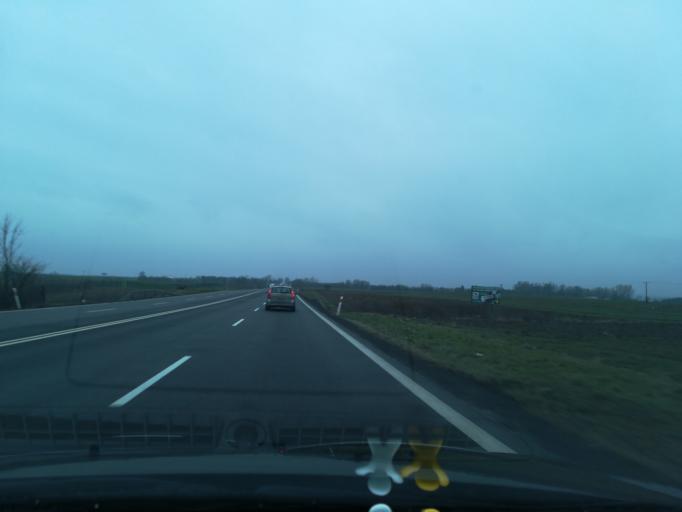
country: PL
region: Subcarpathian Voivodeship
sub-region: Powiat lancucki
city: Kosina
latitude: 50.0753
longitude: 22.3072
